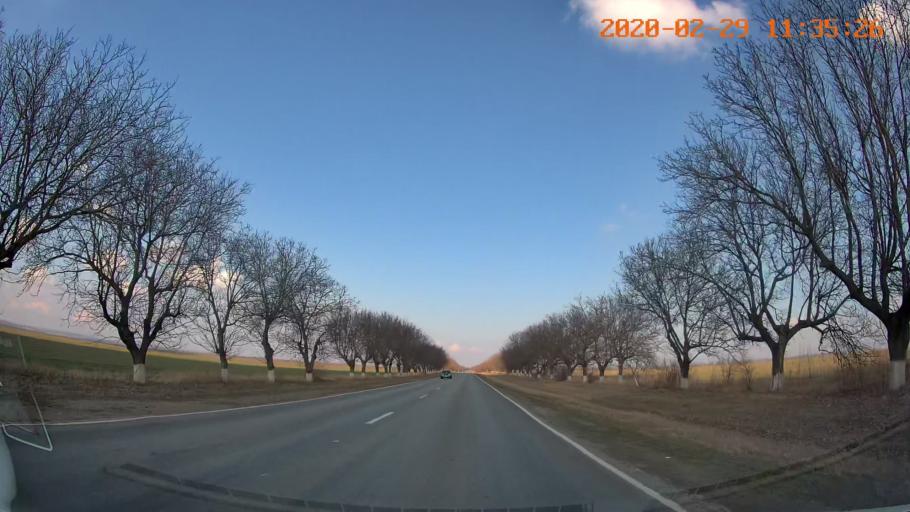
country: MD
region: Rezina
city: Saharna
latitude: 47.5804
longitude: 29.0634
